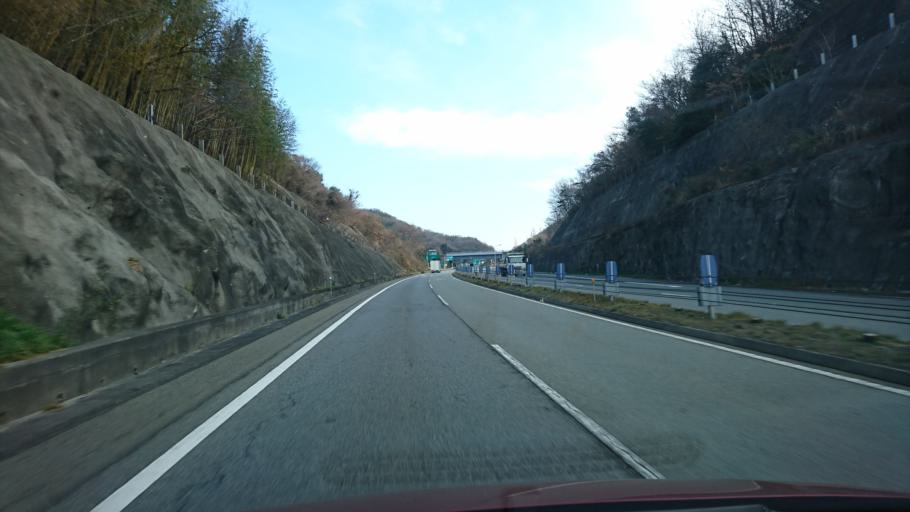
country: JP
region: Hyogo
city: Himeji
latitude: 34.8531
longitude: 134.7344
